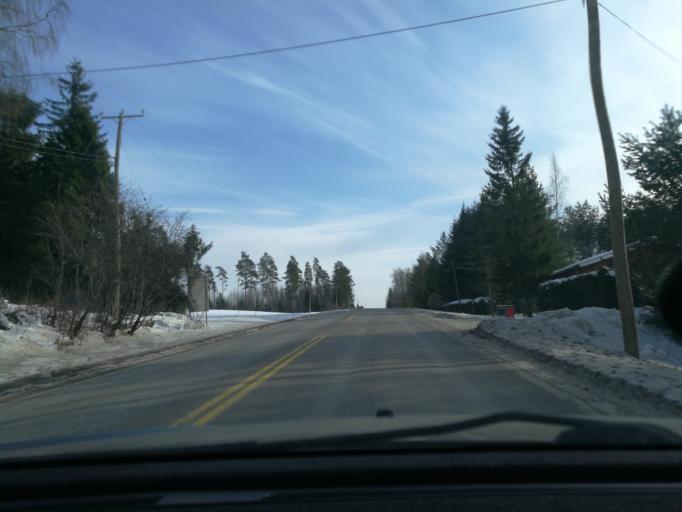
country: FI
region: Uusimaa
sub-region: Helsinki
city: Saukkola
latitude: 60.3997
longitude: 24.0667
